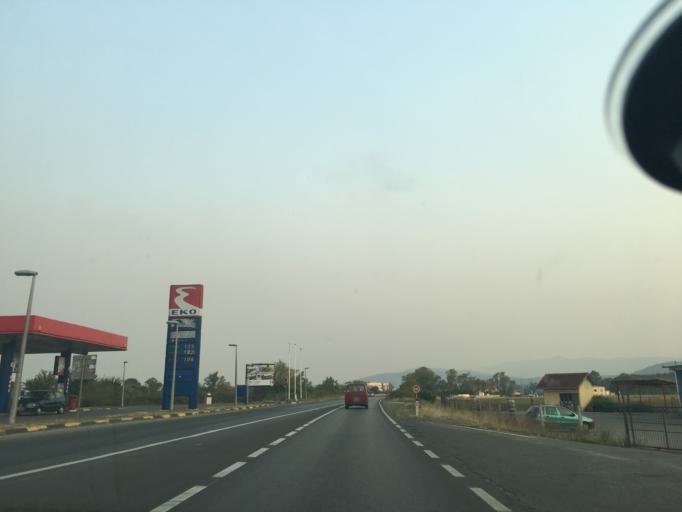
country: ME
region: Danilovgrad
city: Danilovgrad
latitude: 42.5382
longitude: 19.1123
